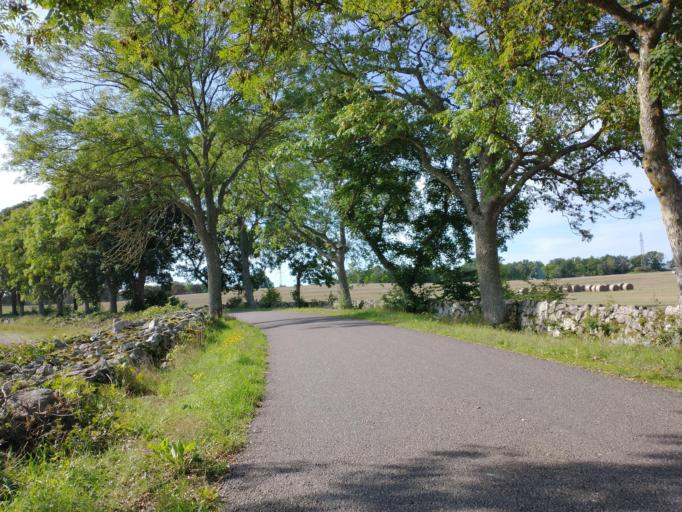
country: SE
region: Kalmar
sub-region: Kalmar Kommun
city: Lindsdal
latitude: 56.7801
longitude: 16.3208
